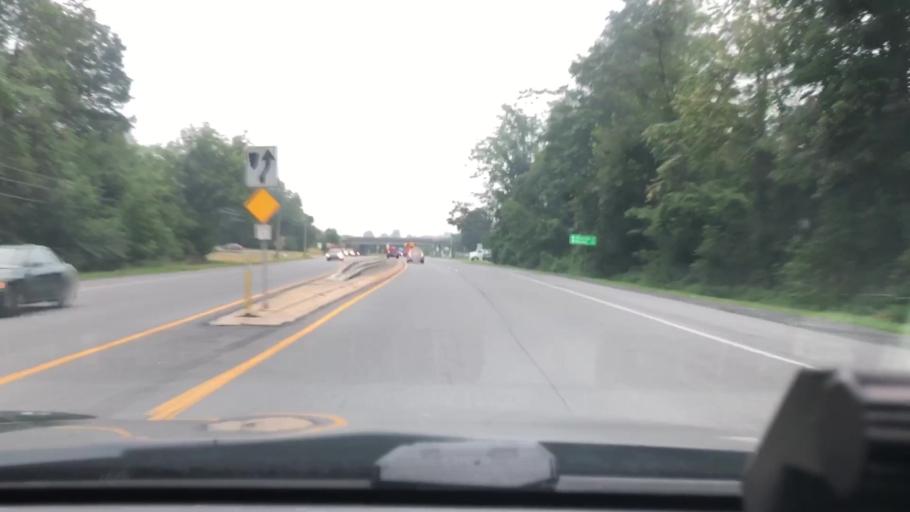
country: US
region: Pennsylvania
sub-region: Berks County
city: Kutztown
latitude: 40.5298
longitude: -75.7823
